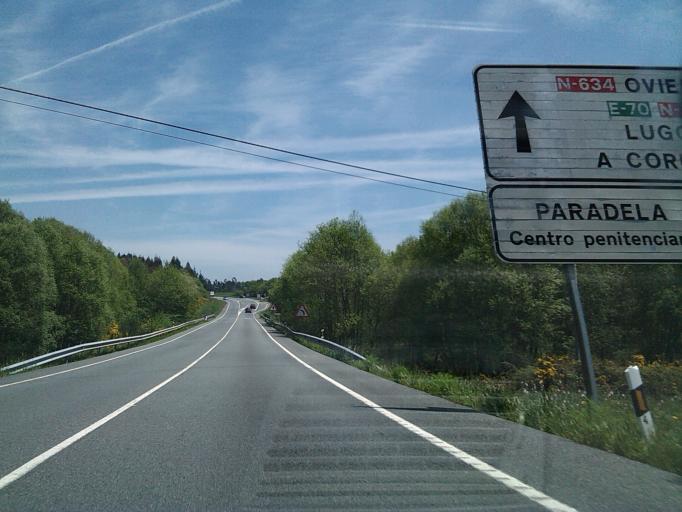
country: ES
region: Galicia
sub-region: Provincia da Coruna
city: Aranga
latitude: 43.1657
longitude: -7.9895
